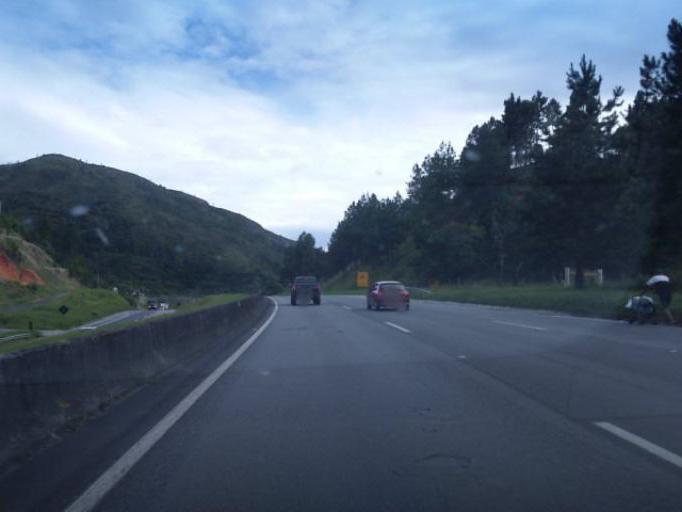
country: BR
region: Parana
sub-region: Campina Grande Do Sul
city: Campina Grande do Sul
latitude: -25.1361
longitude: -48.8572
